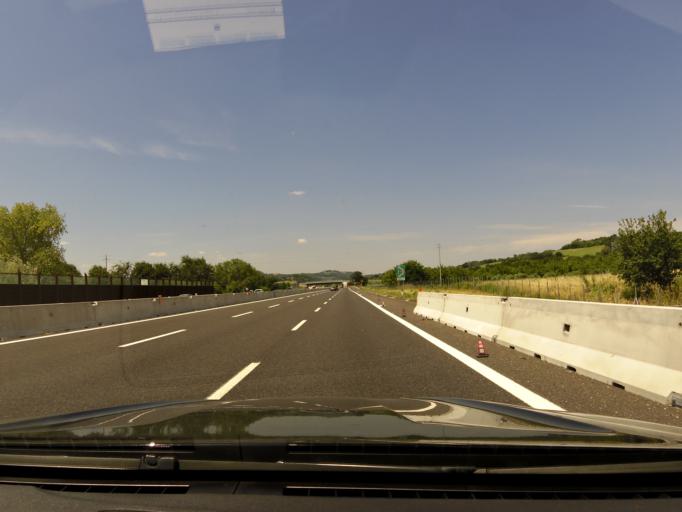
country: IT
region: The Marches
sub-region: Provincia di Pesaro e Urbino
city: Centinarola
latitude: 43.8380
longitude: 12.9881
